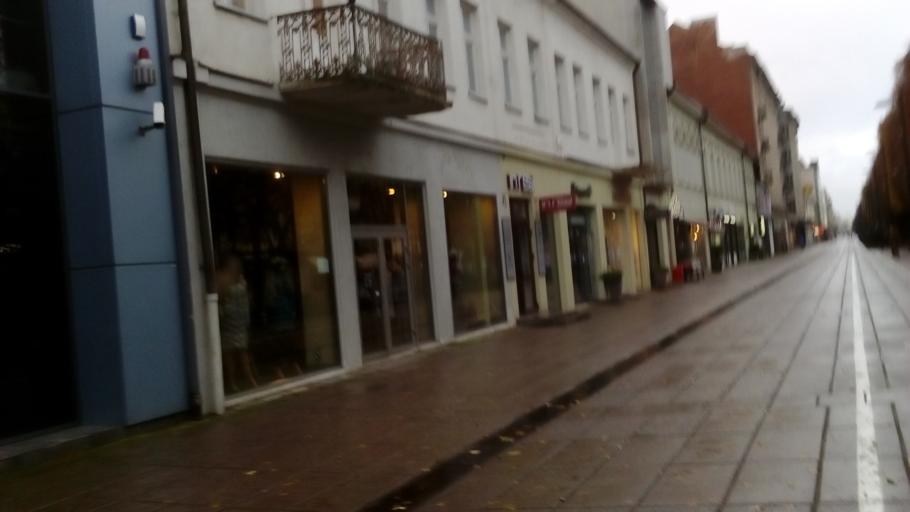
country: LT
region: Kauno apskritis
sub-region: Kaunas
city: Kaunas
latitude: 54.8961
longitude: 23.9166
